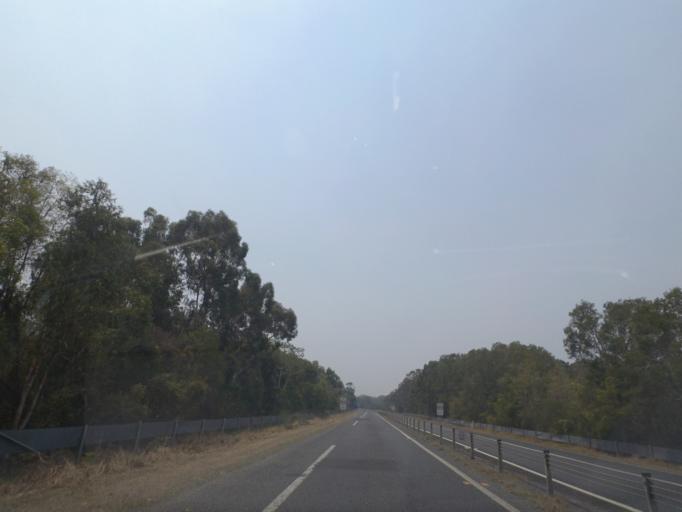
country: AU
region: New South Wales
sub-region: Ballina
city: Ballina
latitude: -28.9321
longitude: 153.4736
